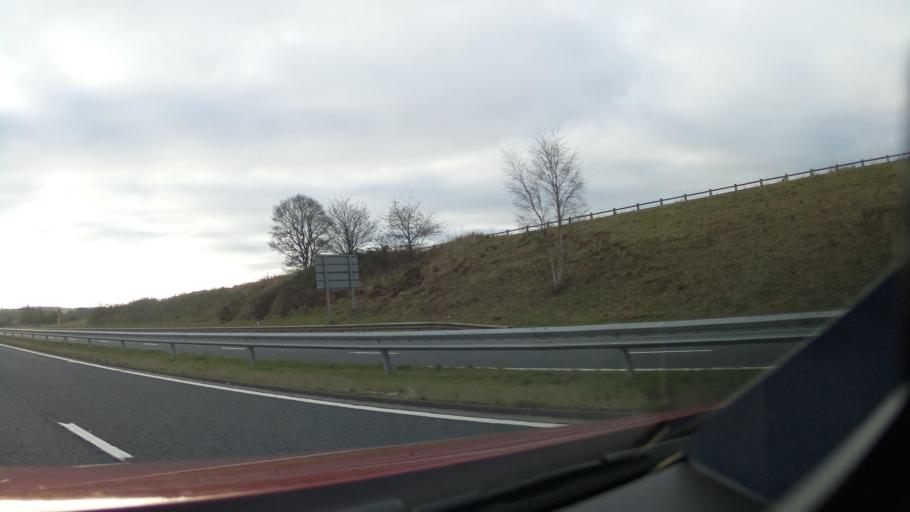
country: GB
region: England
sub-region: Cumbria
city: Scotby
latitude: 54.8649
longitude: -2.8761
